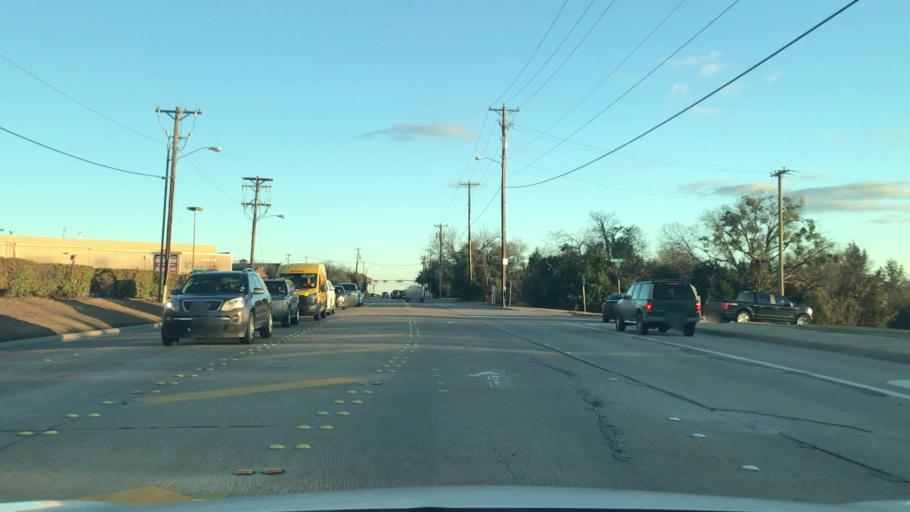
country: US
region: Texas
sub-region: Rockwall County
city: Rockwall
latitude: 32.8939
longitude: -96.4738
